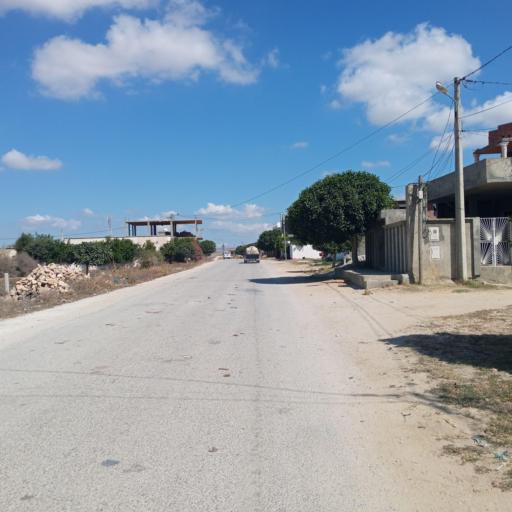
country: TN
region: Nabul
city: Qulaybiyah
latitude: 36.8550
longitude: 11.0366
